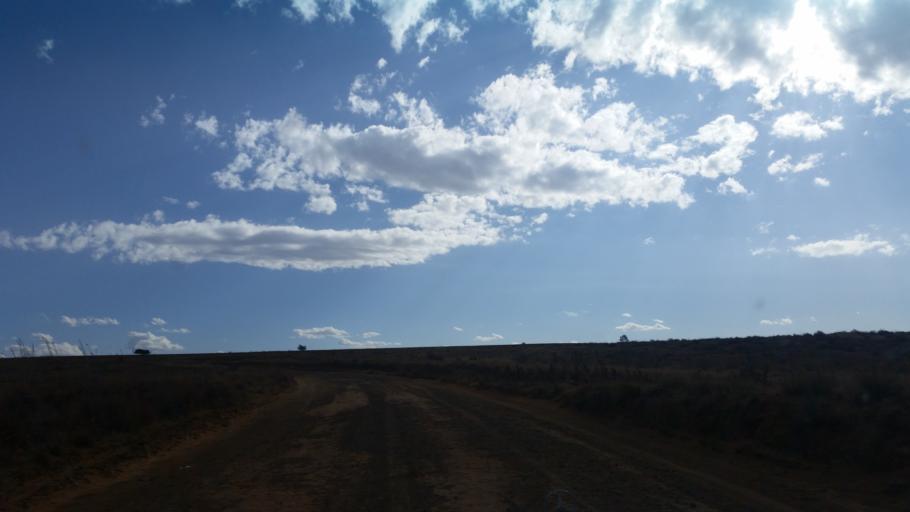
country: ZA
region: Orange Free State
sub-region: Thabo Mofutsanyana District Municipality
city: Phuthaditjhaba
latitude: -28.3507
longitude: 28.6060
